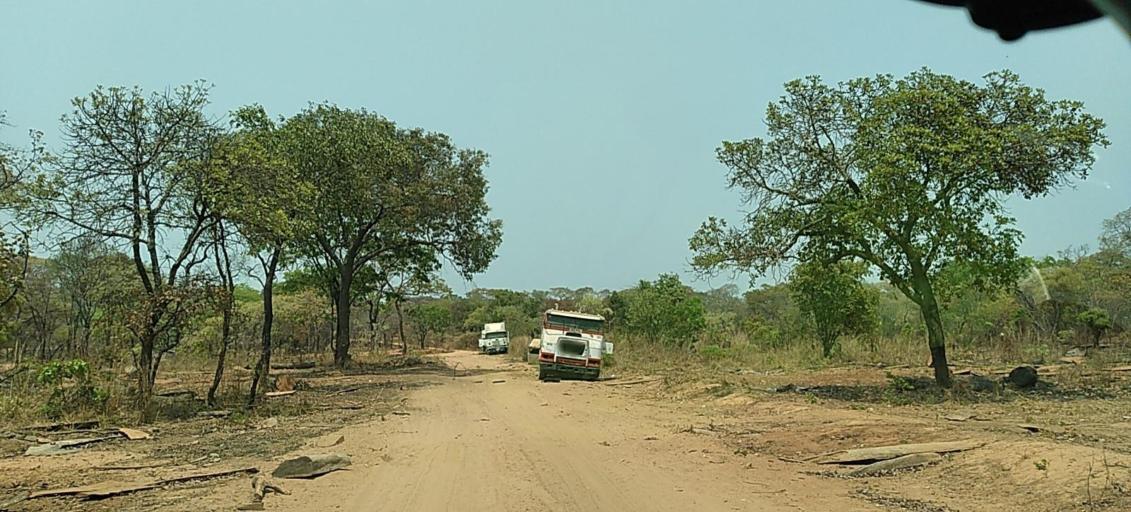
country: ZM
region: North-Western
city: Kabompo
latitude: -13.7110
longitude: 24.3271
